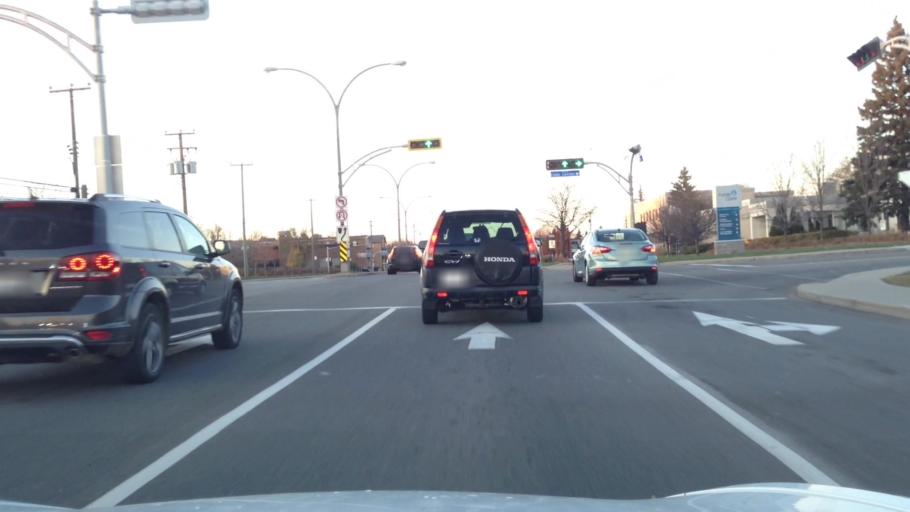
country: CA
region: Quebec
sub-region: Montreal
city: Pointe-Claire
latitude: 45.4472
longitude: -73.8169
